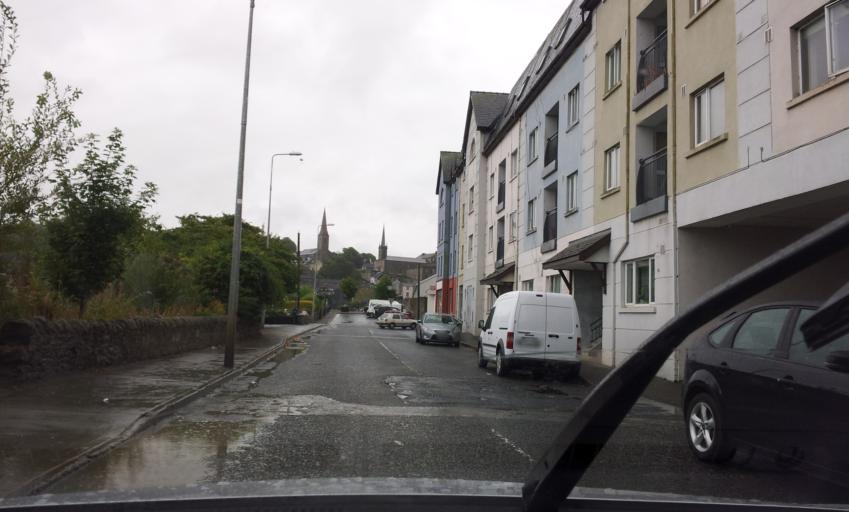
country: IE
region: Leinster
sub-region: Loch Garman
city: New Ross
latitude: 52.3978
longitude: -6.9489
